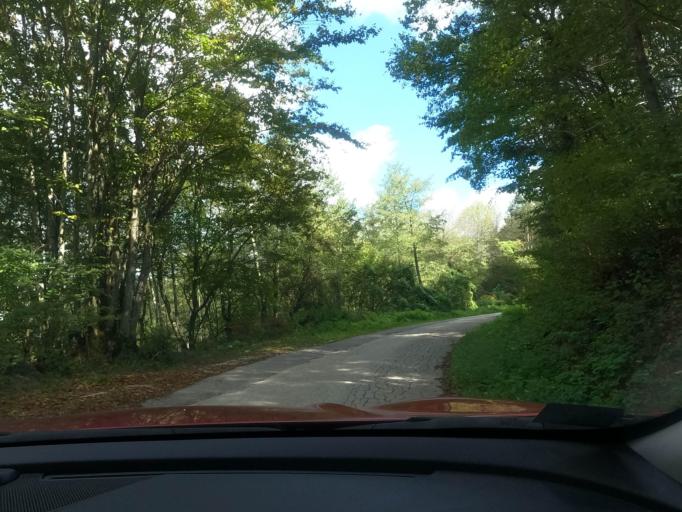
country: BA
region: Federation of Bosnia and Herzegovina
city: Velika Kladusa
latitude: 45.2386
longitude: 15.7564
